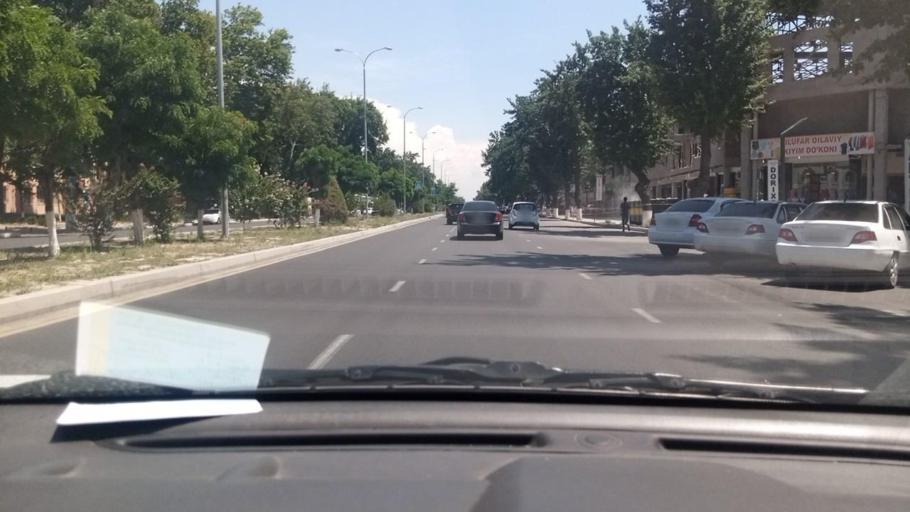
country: UZ
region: Toshkent Shahri
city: Tashkent
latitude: 41.2879
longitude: 69.2032
